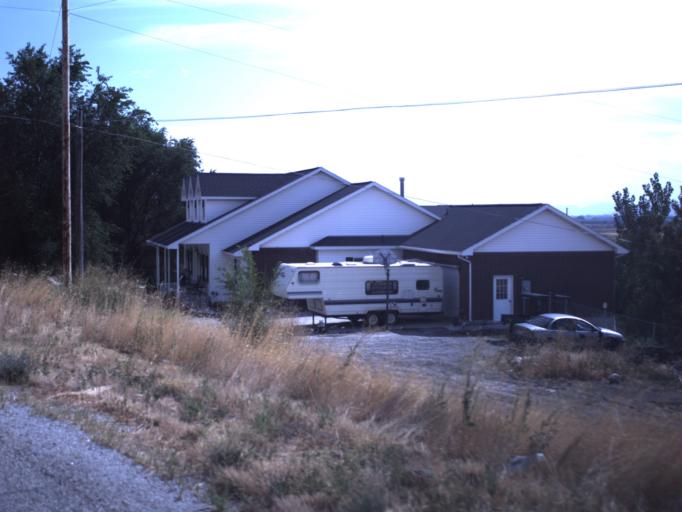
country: US
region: Utah
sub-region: Box Elder County
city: Elwood
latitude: 41.7243
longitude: -112.0958
